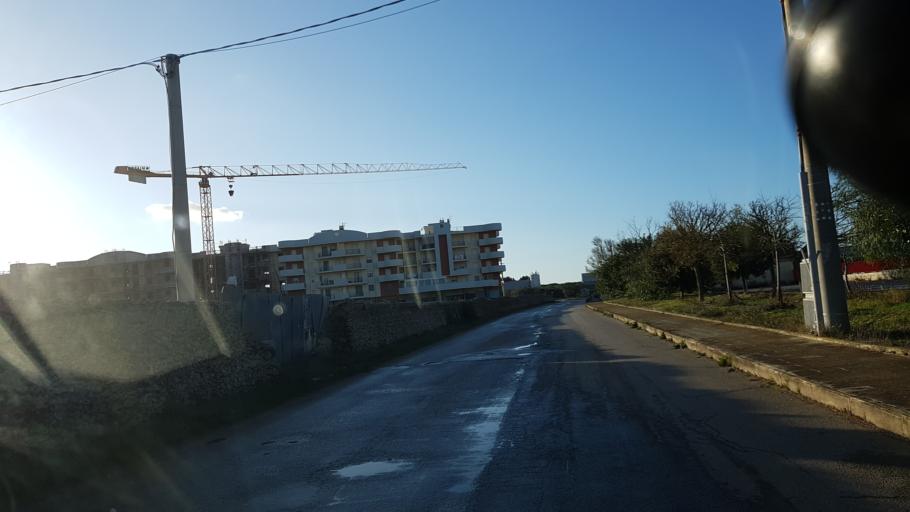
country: IT
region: Apulia
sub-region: Provincia di Bari
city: Gioia del Colle
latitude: 40.8017
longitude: 16.9067
